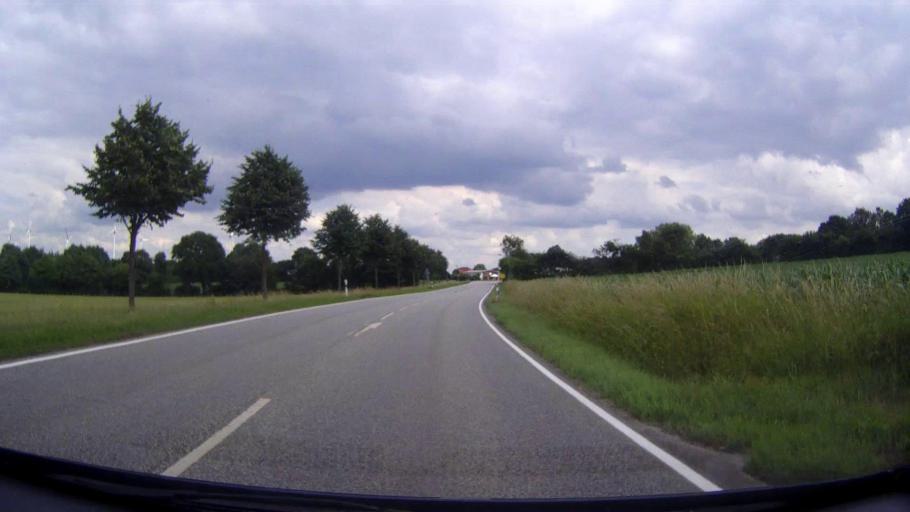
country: DE
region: Schleswig-Holstein
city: Gokels
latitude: 54.1162
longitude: 9.4619
